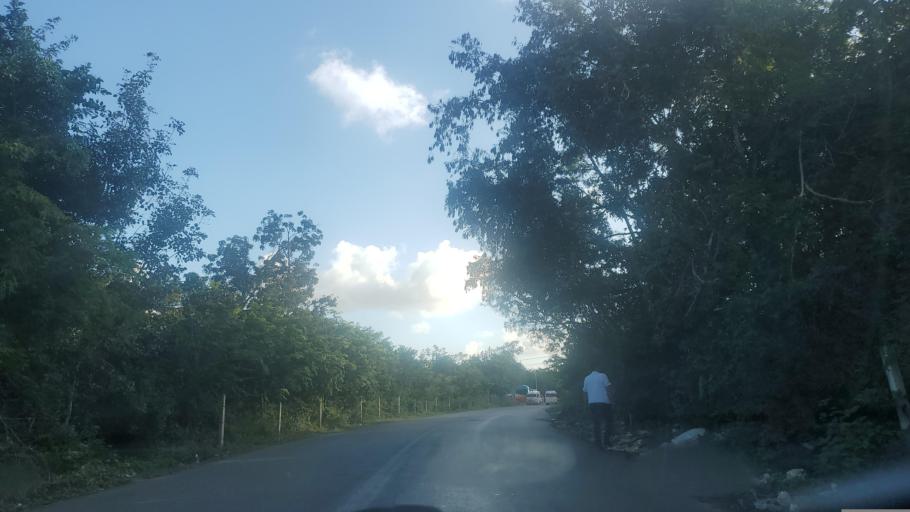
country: MX
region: Quintana Roo
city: Tulum
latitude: 20.2169
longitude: -87.4559
